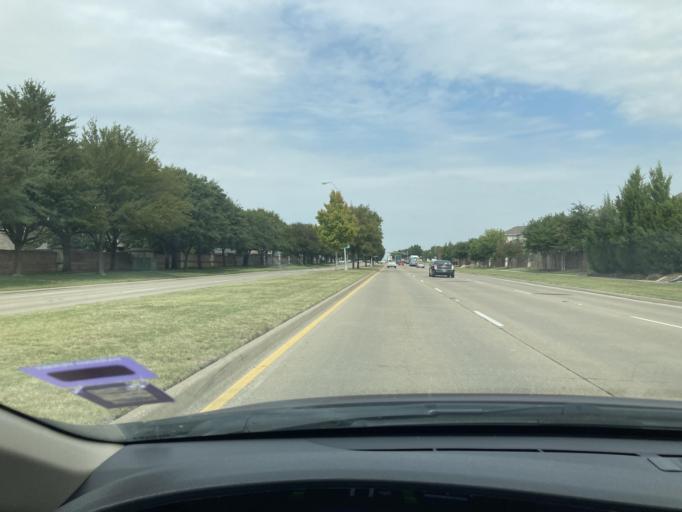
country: US
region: Texas
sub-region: Dallas County
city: Addison
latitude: 33.0392
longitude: -96.7945
